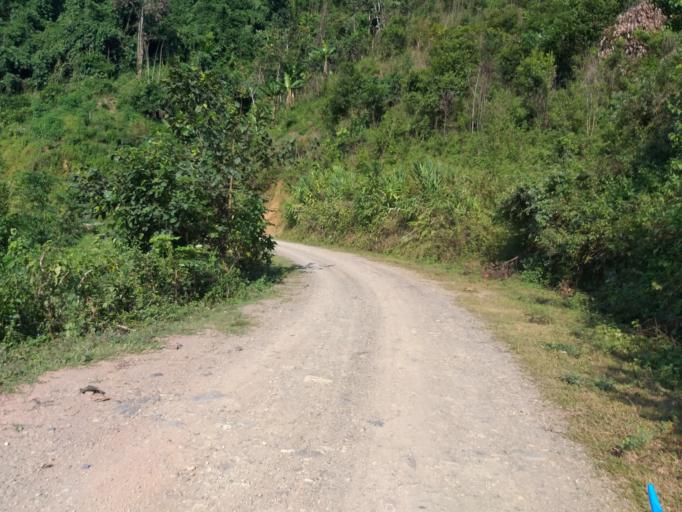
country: LA
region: Phongsali
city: Khoa
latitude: 21.1979
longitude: 102.6653
